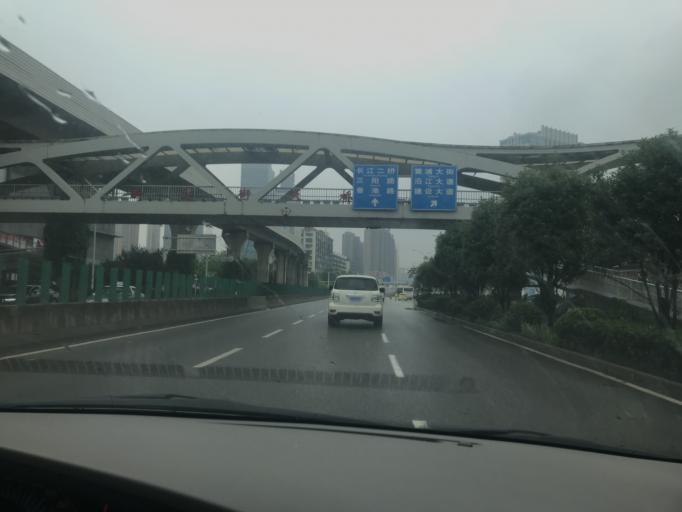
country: CN
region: Hubei
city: Jiang'an
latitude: 30.6199
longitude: 114.3081
